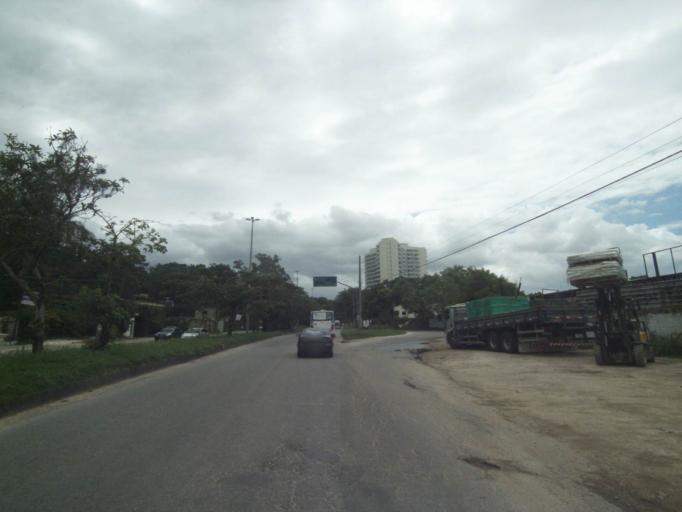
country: BR
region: Rio de Janeiro
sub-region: Nilopolis
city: Nilopolis
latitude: -22.9770
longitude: -43.4166
